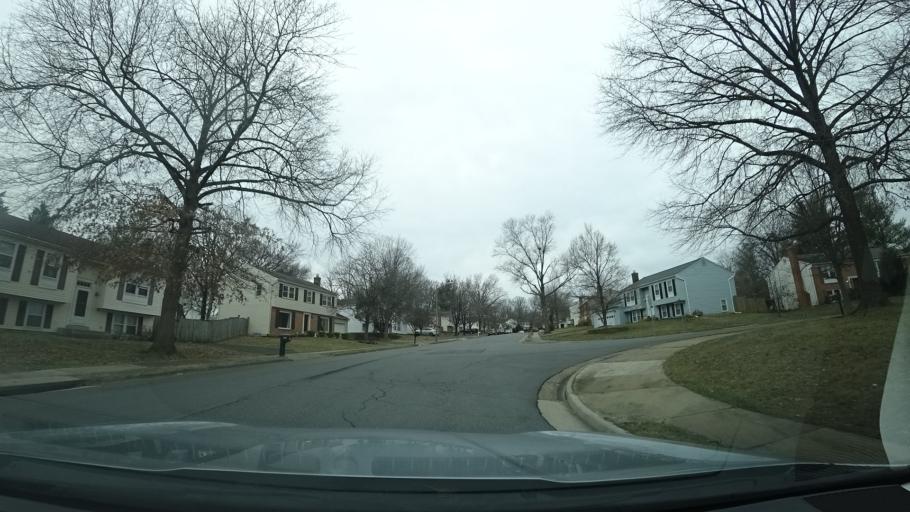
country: US
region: Virginia
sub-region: Fairfax County
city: Herndon
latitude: 38.9768
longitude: -77.3727
